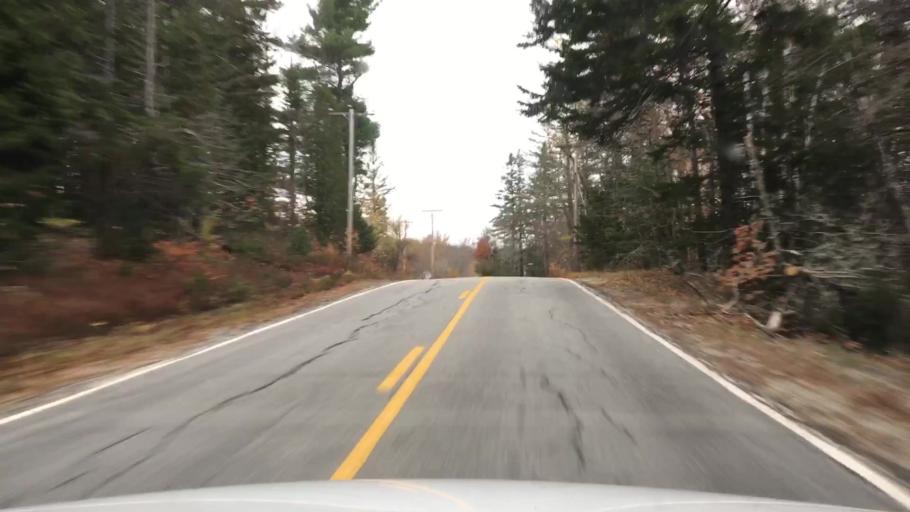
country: US
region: Maine
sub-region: Hancock County
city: Sedgwick
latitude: 44.2999
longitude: -68.5595
